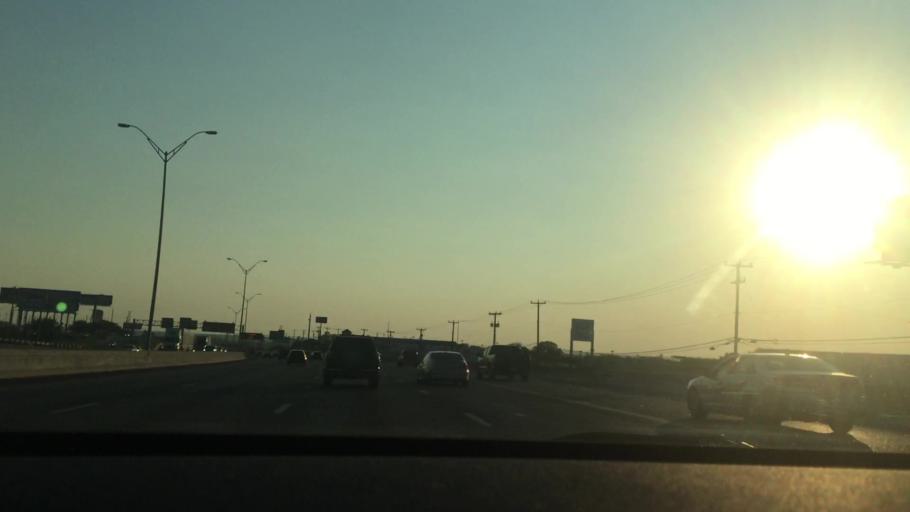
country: US
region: Texas
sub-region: Bexar County
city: Live Oak
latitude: 29.5513
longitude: -98.3589
